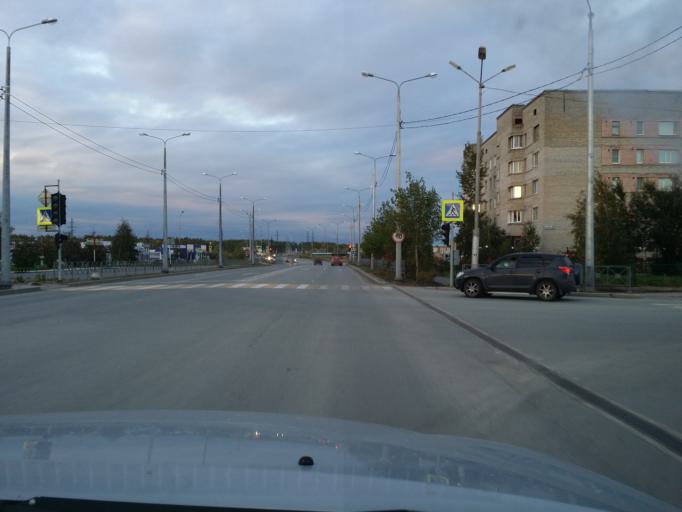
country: RU
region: Khanty-Mansiyskiy Avtonomnyy Okrug
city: Megion
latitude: 61.0400
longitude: 76.1026
